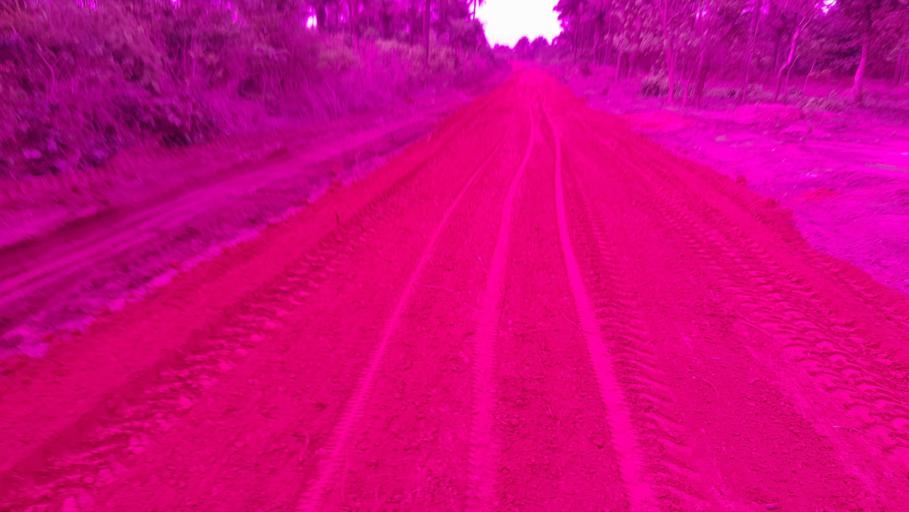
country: GN
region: Boke
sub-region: Boffa
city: Boffa
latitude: 10.0326
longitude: -13.8776
